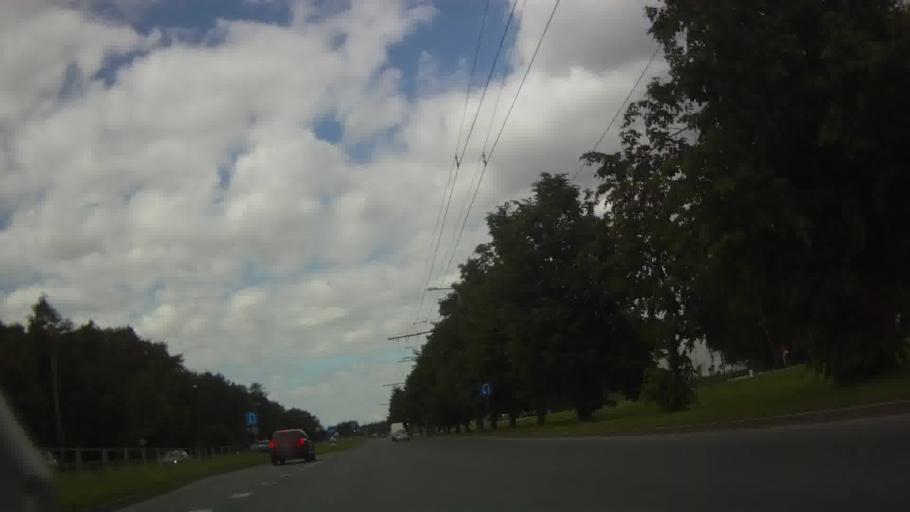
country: LV
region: Stopini
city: Ulbroka
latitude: 56.9432
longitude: 24.2055
